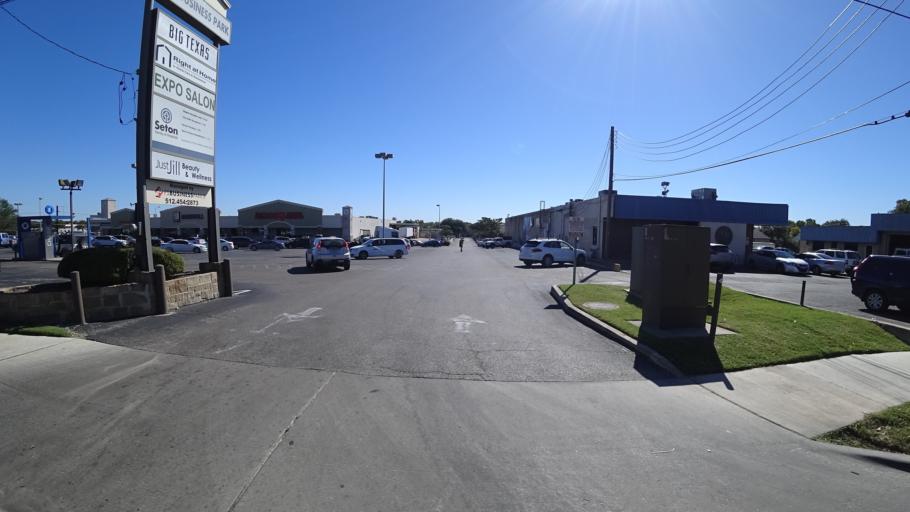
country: US
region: Texas
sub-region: Travis County
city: Austin
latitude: 30.3238
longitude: -97.7276
